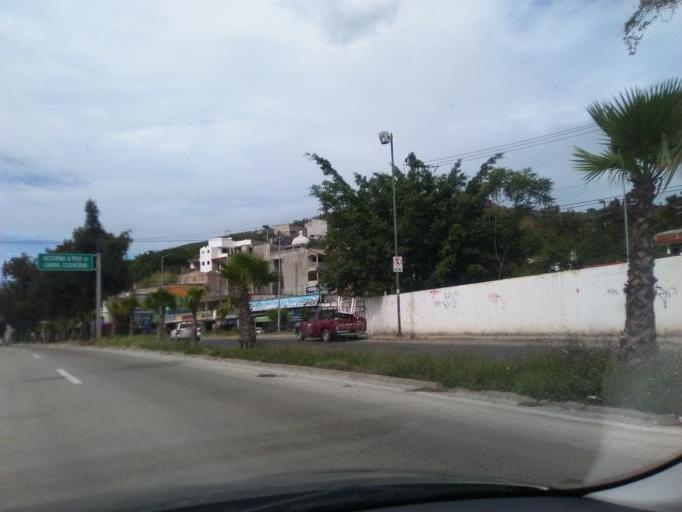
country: MX
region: Guerrero
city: Chilpancingo de los Bravos
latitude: 17.5683
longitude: -99.5115
